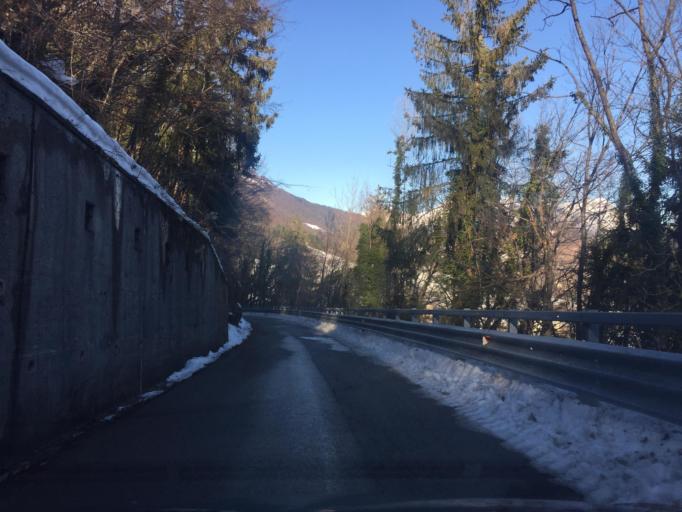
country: IT
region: Friuli Venezia Giulia
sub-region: Provincia di Udine
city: Chiaulis
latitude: 46.4221
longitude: 12.9896
